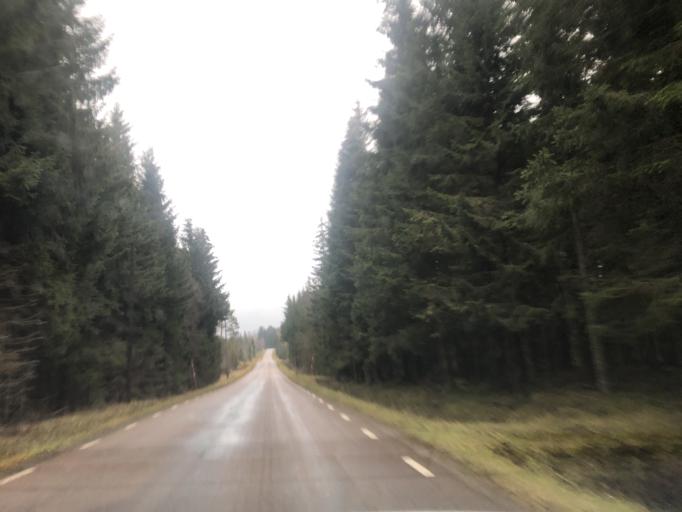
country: SE
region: Vaestra Goetaland
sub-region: Ulricehamns Kommun
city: Ulricehamn
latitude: 57.8270
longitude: 13.5095
